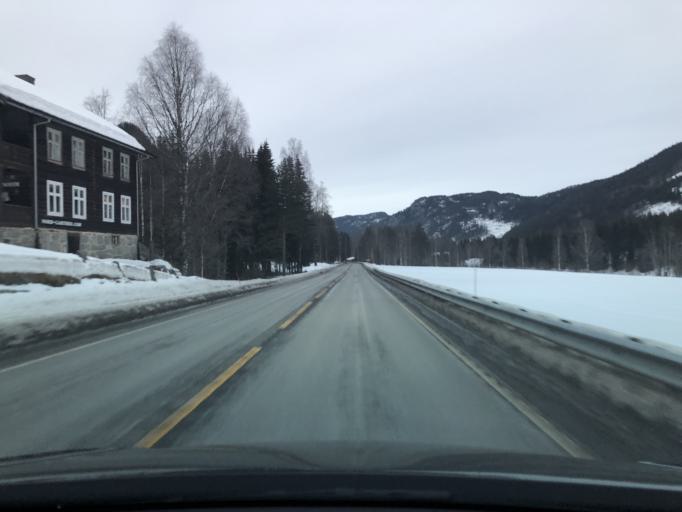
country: NO
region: Oppland
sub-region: Etnedal
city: Bruflat
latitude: 60.7105
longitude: 9.7088
